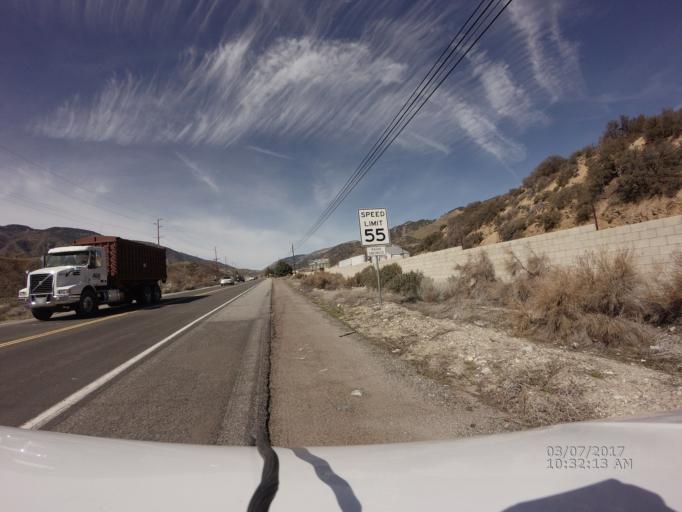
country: US
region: California
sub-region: Kern County
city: Lebec
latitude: 34.8179
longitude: -118.8915
